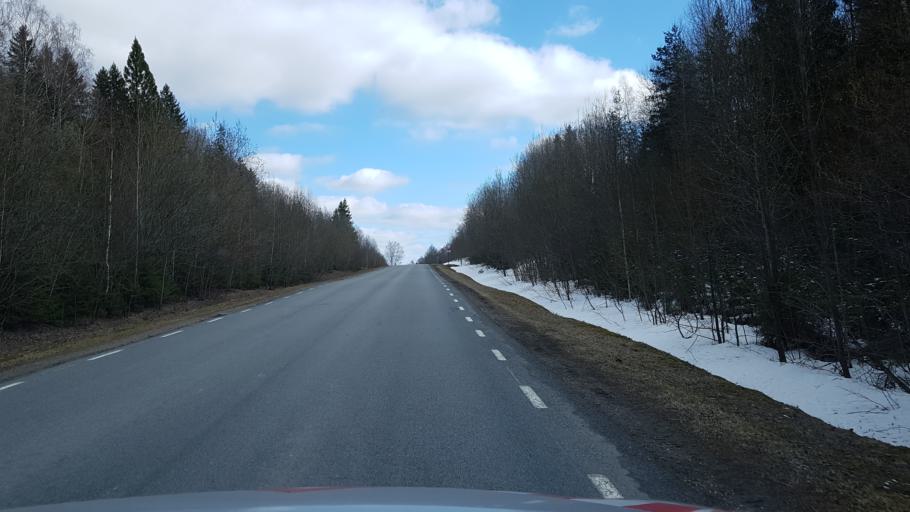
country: EE
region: Laeaene-Virumaa
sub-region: Tamsalu vald
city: Tamsalu
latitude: 59.1647
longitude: 26.0785
